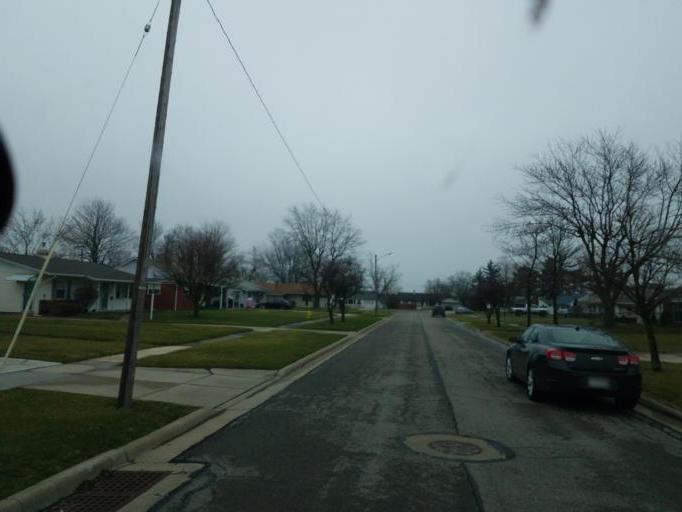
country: US
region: Ohio
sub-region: Richland County
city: Ontario
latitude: 40.7731
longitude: -82.5870
